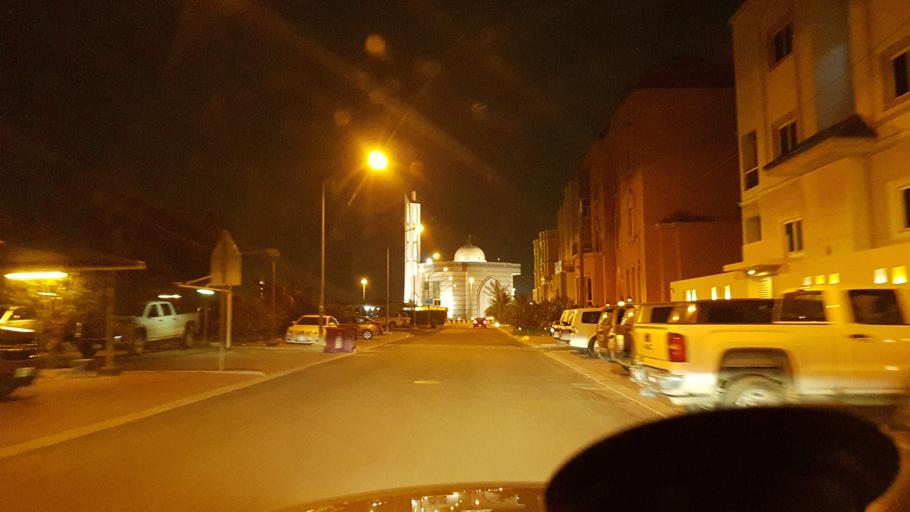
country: KW
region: Al Ahmadi
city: Al Manqaf
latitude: 29.1177
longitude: 48.1271
